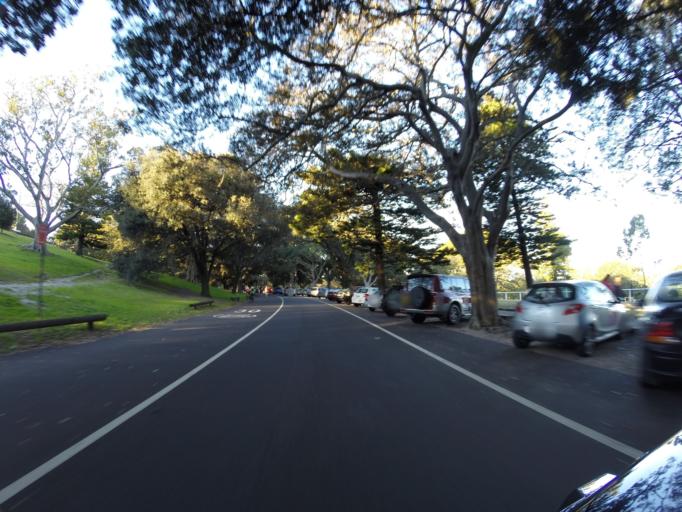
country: AU
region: New South Wales
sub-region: Woollahra
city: Woollahra
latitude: -33.8972
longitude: 151.2290
